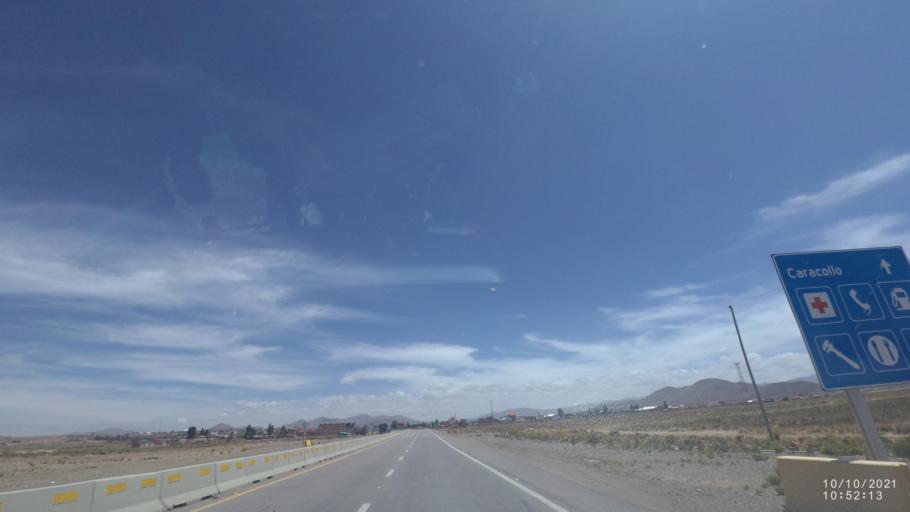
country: BO
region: La Paz
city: Colquiri
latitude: -17.6558
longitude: -67.2073
